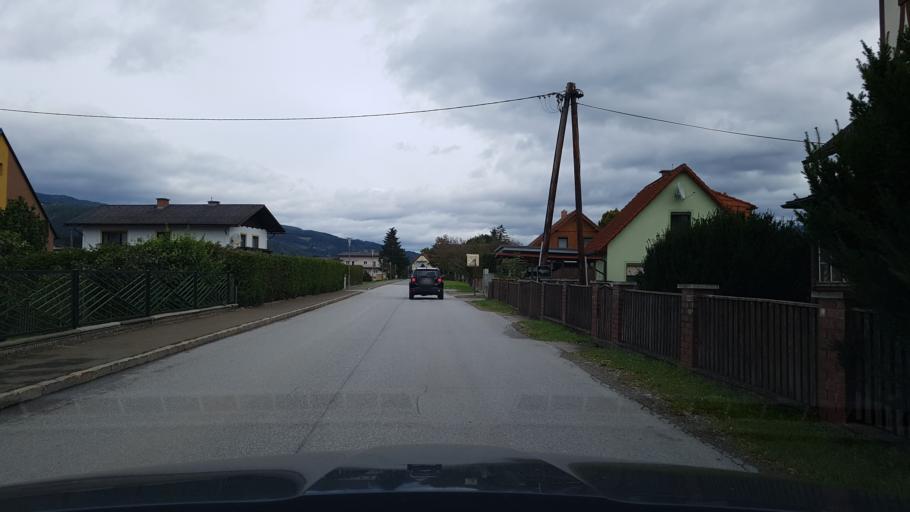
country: AT
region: Styria
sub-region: Politischer Bezirk Bruck-Muerzzuschlag
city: Sankt Marein im Muerztal
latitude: 47.4700
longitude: 15.3682
